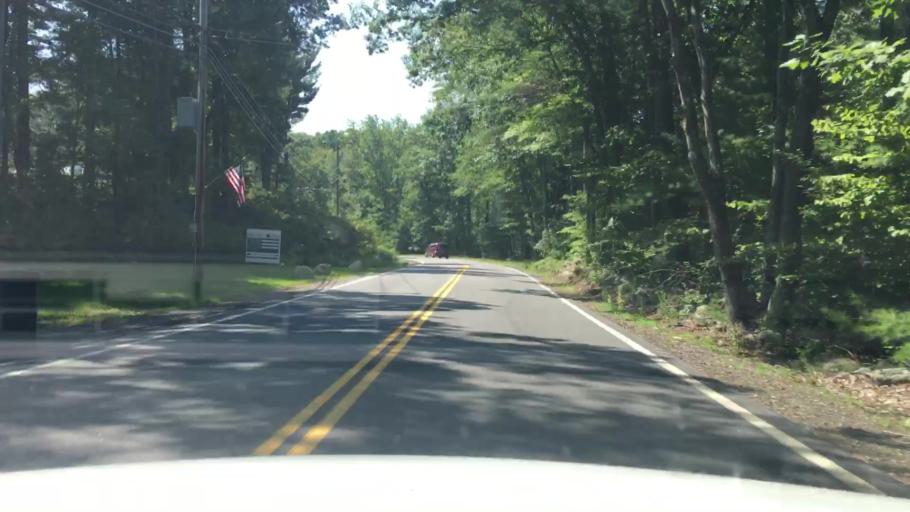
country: US
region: New Hampshire
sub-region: Rockingham County
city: Hampstead
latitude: 42.8830
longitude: -71.1634
